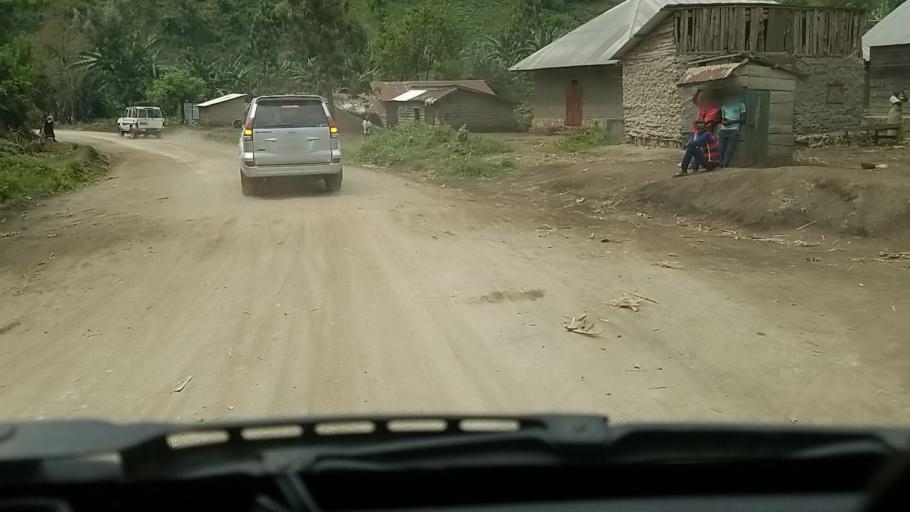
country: CD
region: Nord Kivu
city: Sake
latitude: -1.5912
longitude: 29.0400
